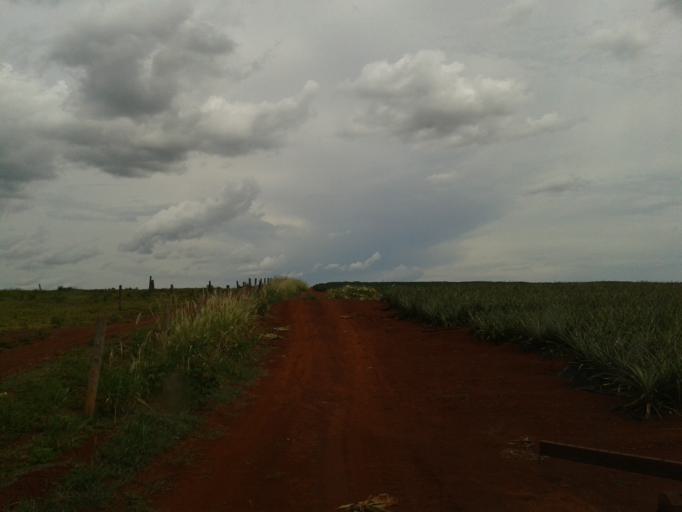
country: BR
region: Minas Gerais
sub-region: Centralina
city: Centralina
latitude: -18.6696
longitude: -49.2359
